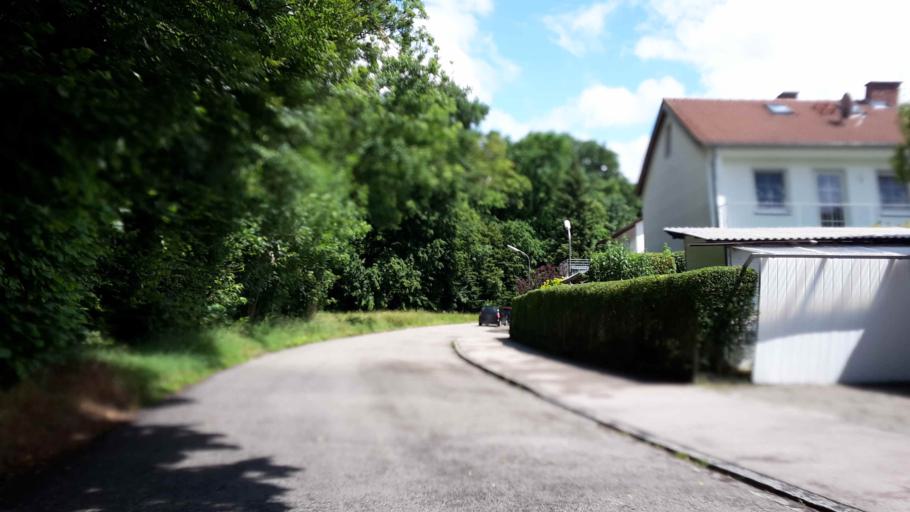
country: DE
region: Bavaria
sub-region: Upper Bavaria
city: Karlsfeld
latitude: 48.1872
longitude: 11.4770
